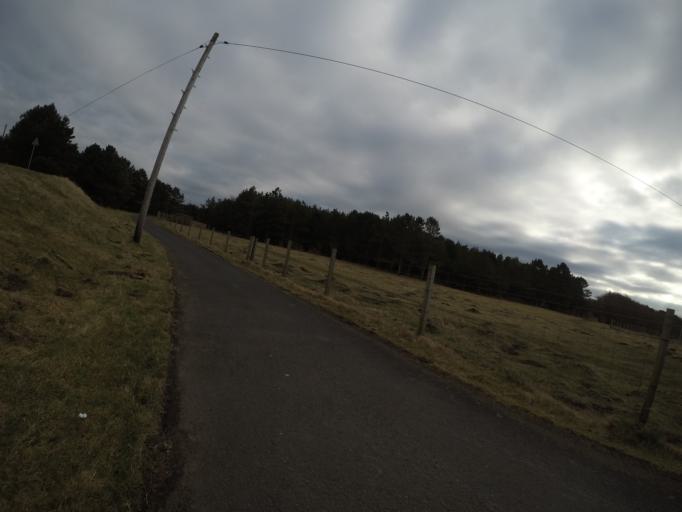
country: GB
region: Scotland
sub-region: North Ayrshire
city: Irvine
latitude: 55.5887
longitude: -4.6622
